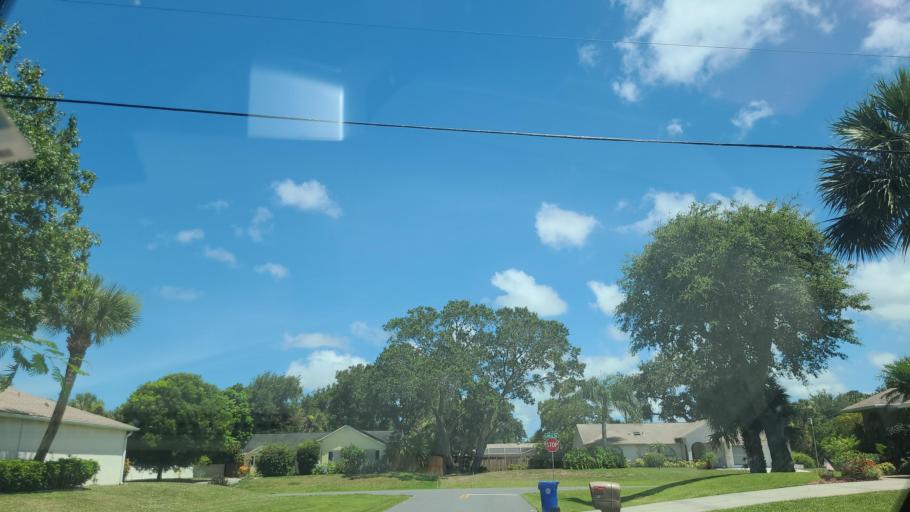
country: US
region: Florida
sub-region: Indian River County
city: Sebastian
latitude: 27.7790
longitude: -80.4802
